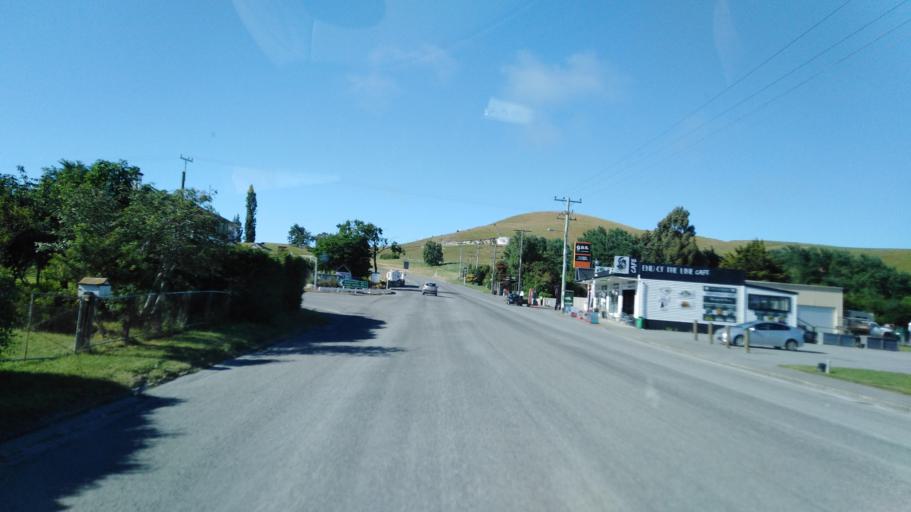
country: NZ
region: Canterbury
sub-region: Hurunui District
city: Amberley
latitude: -42.9697
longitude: 172.7059
